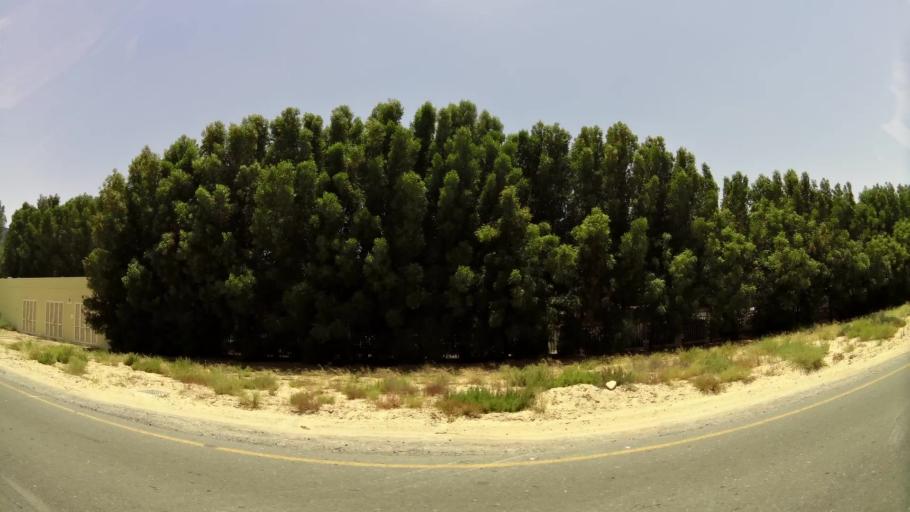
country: AE
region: Dubai
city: Dubai
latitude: 24.9841
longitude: 55.1700
